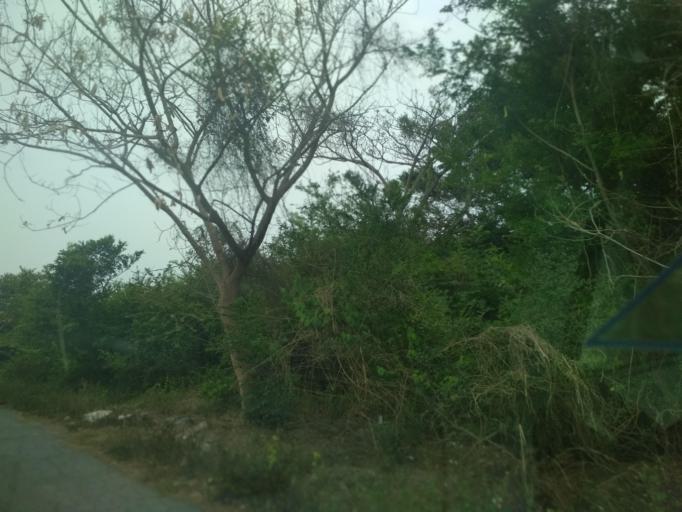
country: MX
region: Veracruz
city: Paso del Toro
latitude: 19.0461
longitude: -96.1492
